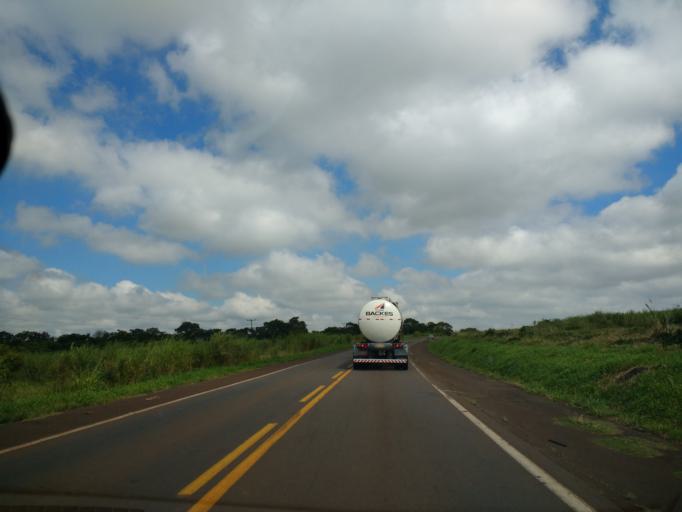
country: BR
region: Parana
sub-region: Cruzeiro Do Oeste
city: Cruzeiro do Oeste
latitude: -23.7706
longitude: -53.0133
